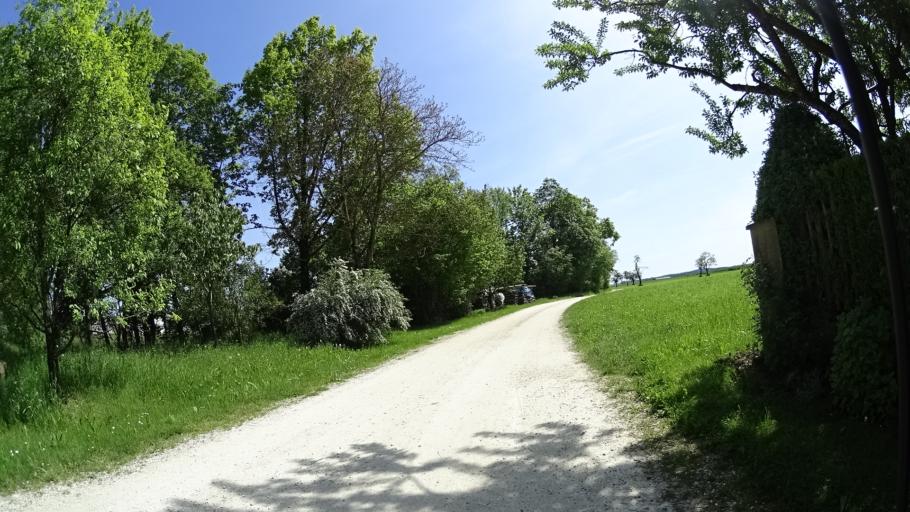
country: DE
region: Bavaria
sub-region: Swabia
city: Pfaffenhofen an der Roth
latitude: 48.3379
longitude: 10.1567
